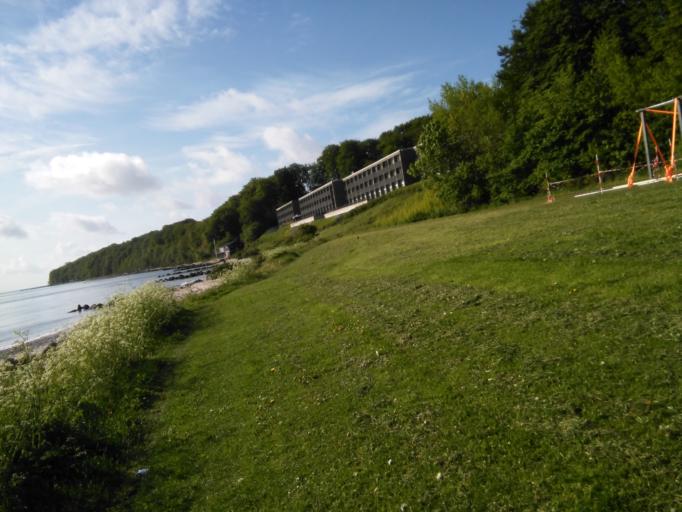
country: DK
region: Central Jutland
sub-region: Arhus Kommune
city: Arhus
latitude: 56.1281
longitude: 10.2146
